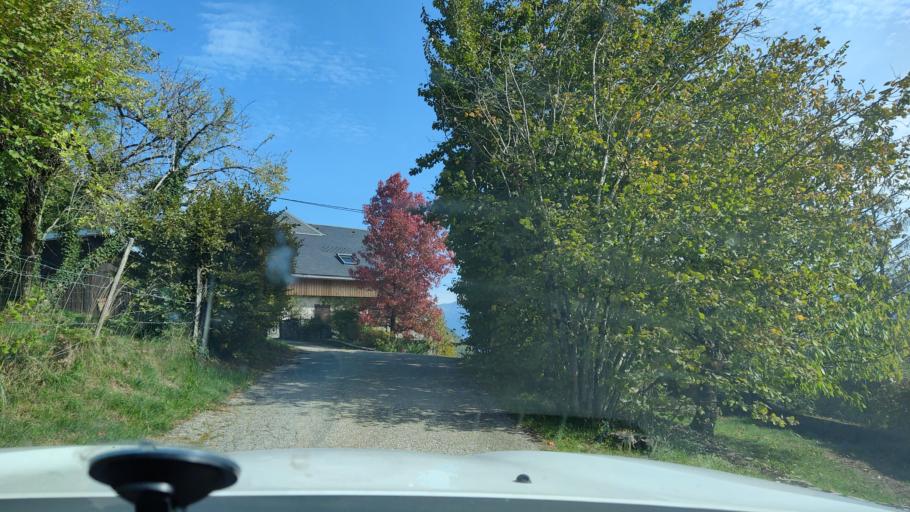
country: FR
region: Rhone-Alpes
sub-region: Departement de la Savoie
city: Coise-Saint-Jean-Pied-Gauthier
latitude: 45.5751
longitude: 6.1436
